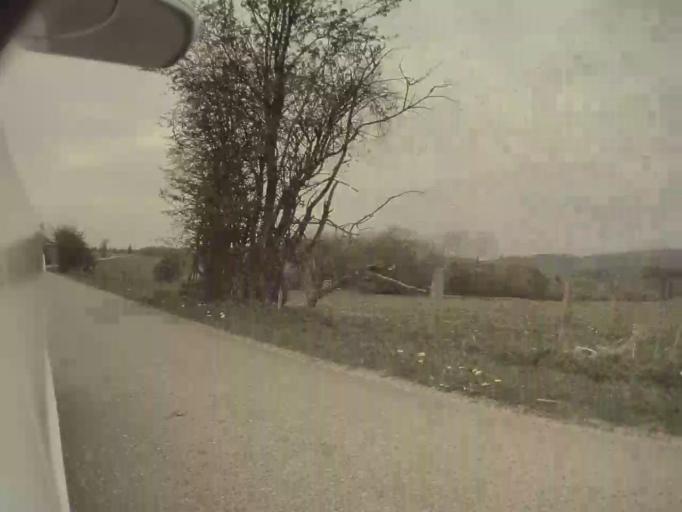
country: BE
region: Wallonia
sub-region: Province du Luxembourg
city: La Roche-en-Ardenne
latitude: 50.2297
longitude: 5.6146
